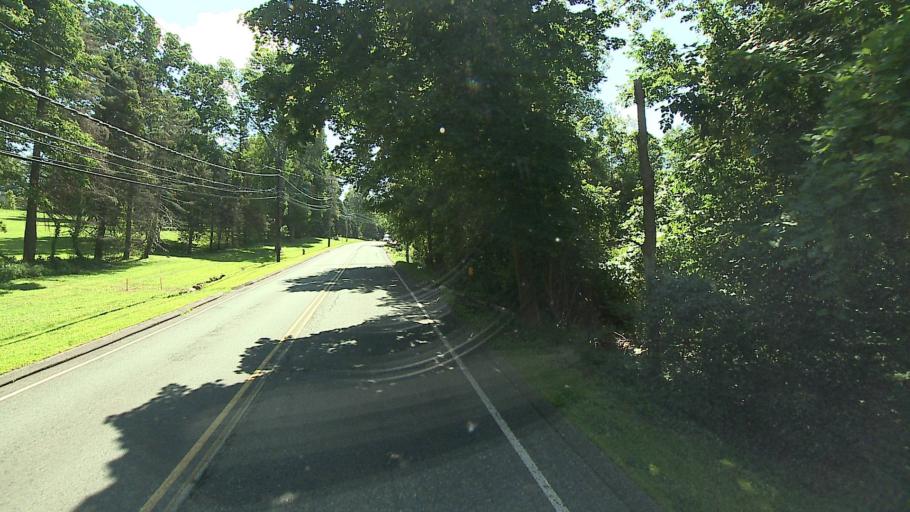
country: US
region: Connecticut
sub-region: New Haven County
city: Oxford
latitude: 41.3774
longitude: -73.1921
